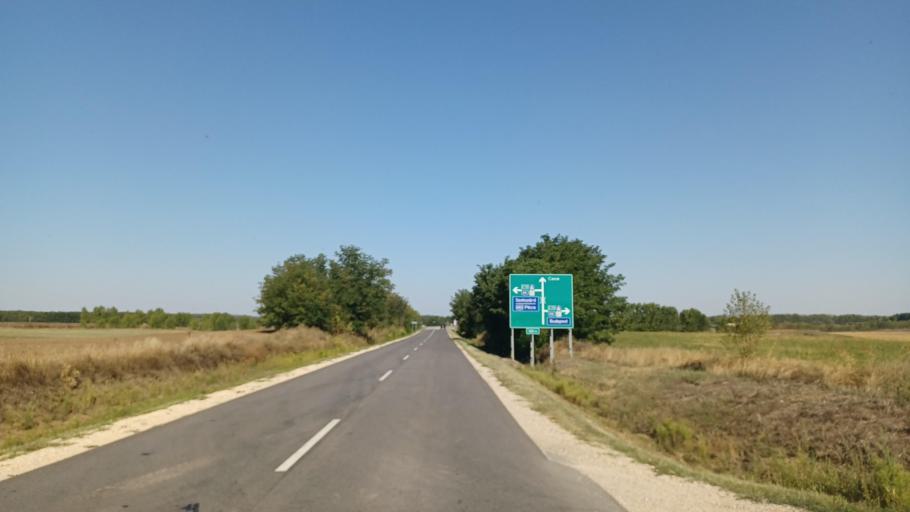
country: HU
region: Tolna
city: Paks
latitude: 46.6687
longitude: 18.8197
